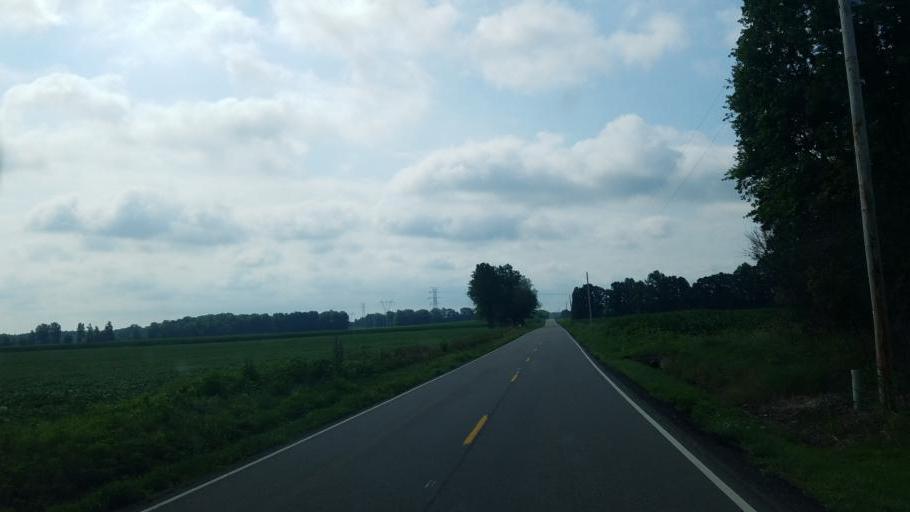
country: US
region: Ohio
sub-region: Knox County
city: Centerburg
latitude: 40.2566
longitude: -82.5948
